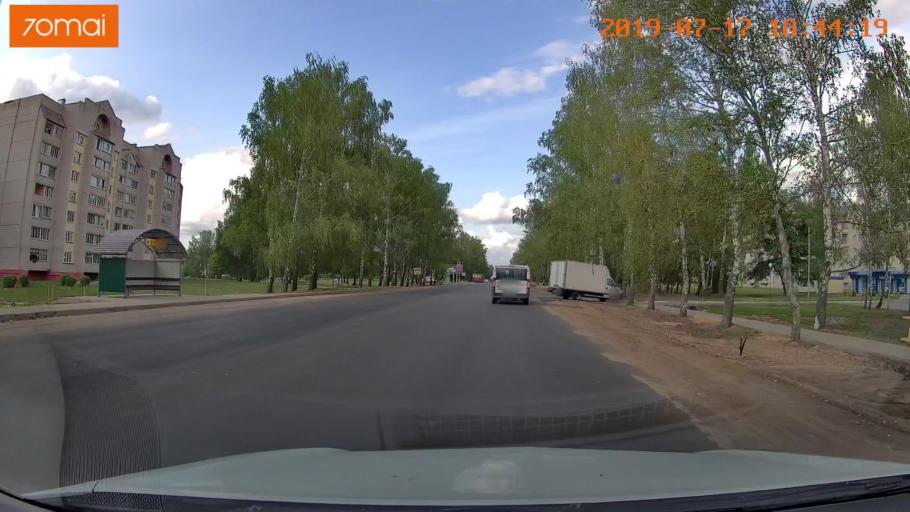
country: BY
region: Mogilev
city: Asipovichy
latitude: 53.3197
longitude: 28.6475
